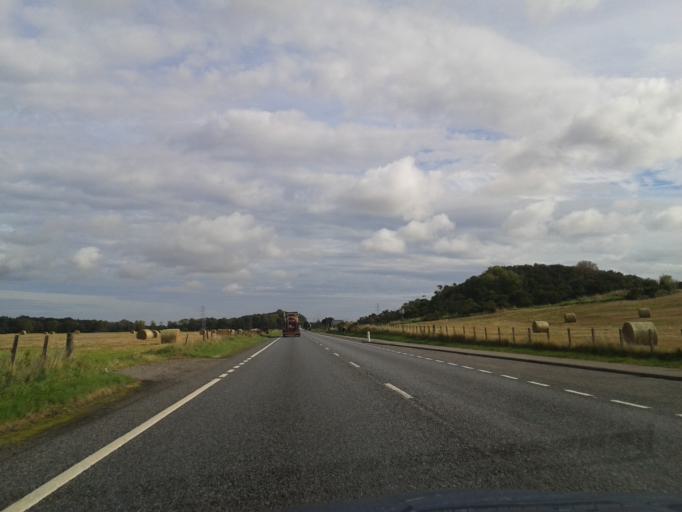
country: GB
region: Scotland
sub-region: Moray
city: Kinloss
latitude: 57.6169
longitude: -3.5842
